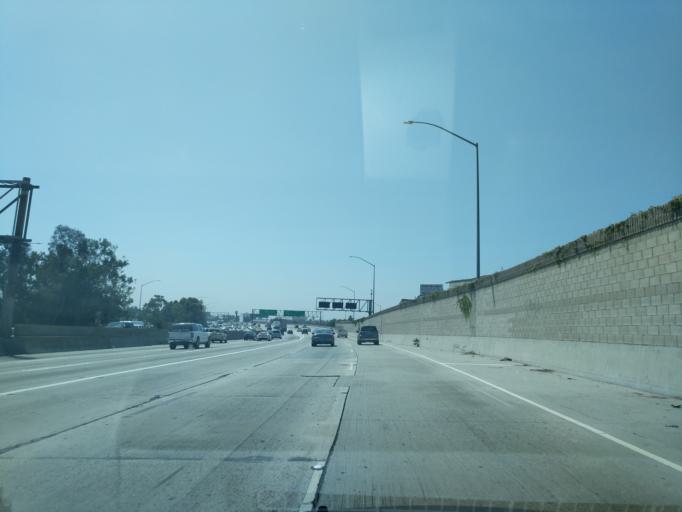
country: US
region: California
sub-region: Los Angeles County
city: Los Angeles
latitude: 34.0462
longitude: -118.2700
